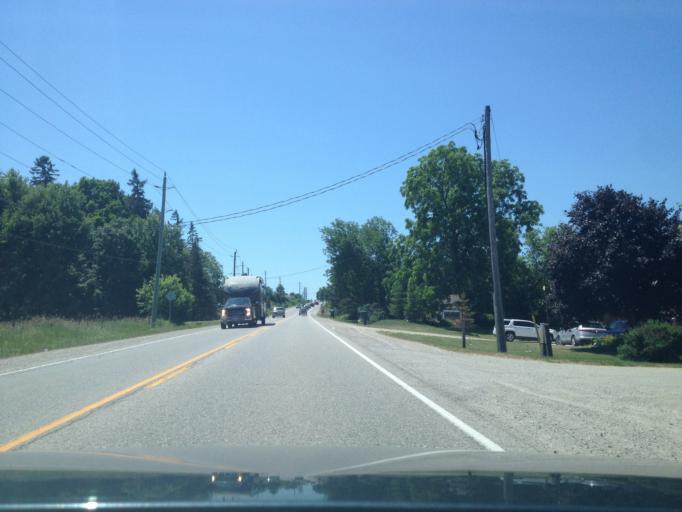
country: CA
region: Ontario
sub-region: Wellington County
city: Guelph
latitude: 43.7132
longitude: -80.3544
